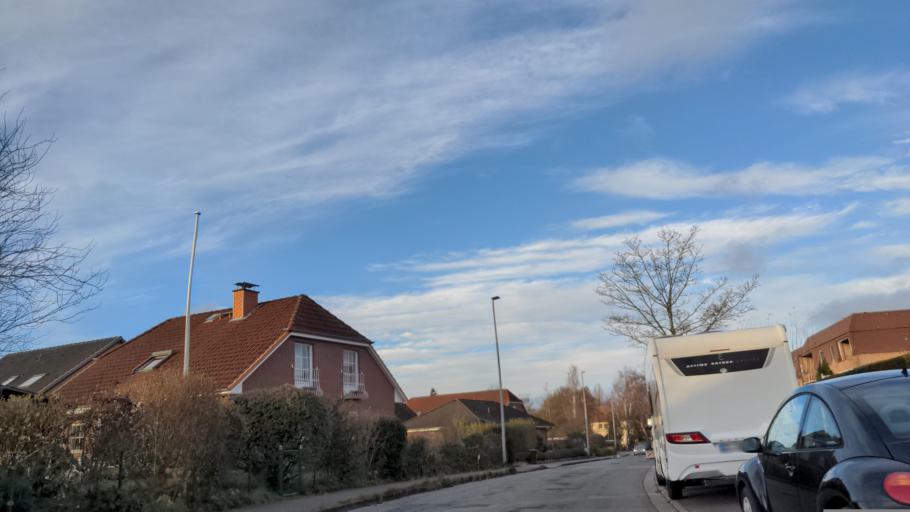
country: DE
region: Schleswig-Holstein
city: Neustadt in Holstein
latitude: 54.0982
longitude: 10.8268
